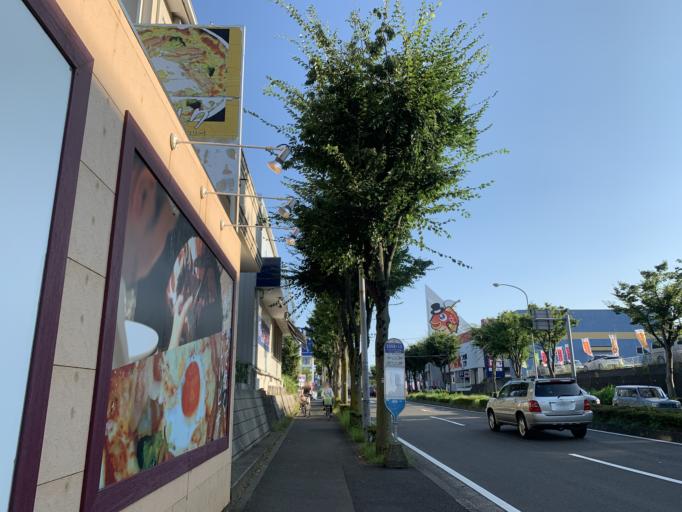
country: JP
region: Tokyo
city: Chofugaoka
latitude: 35.5631
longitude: 139.5803
